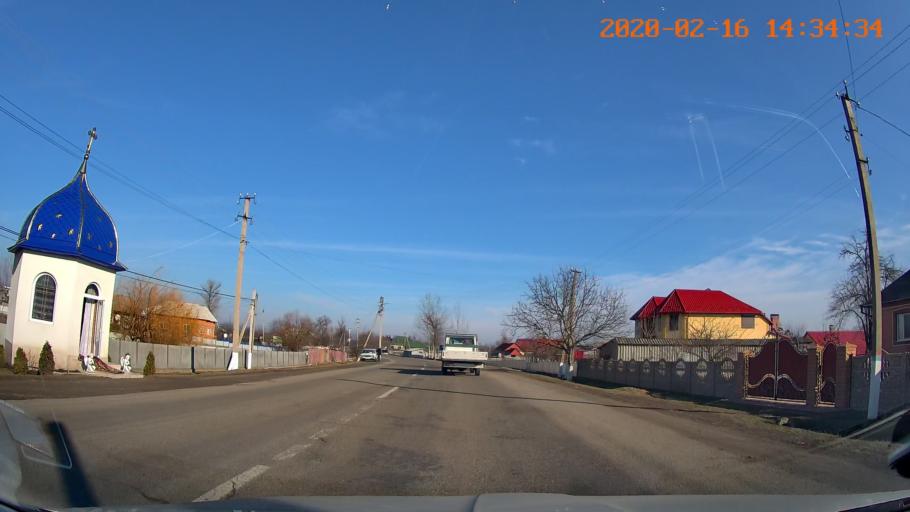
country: RO
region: Botosani
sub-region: Comuna Hudesti
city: Alba
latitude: 48.2209
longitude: 26.4801
